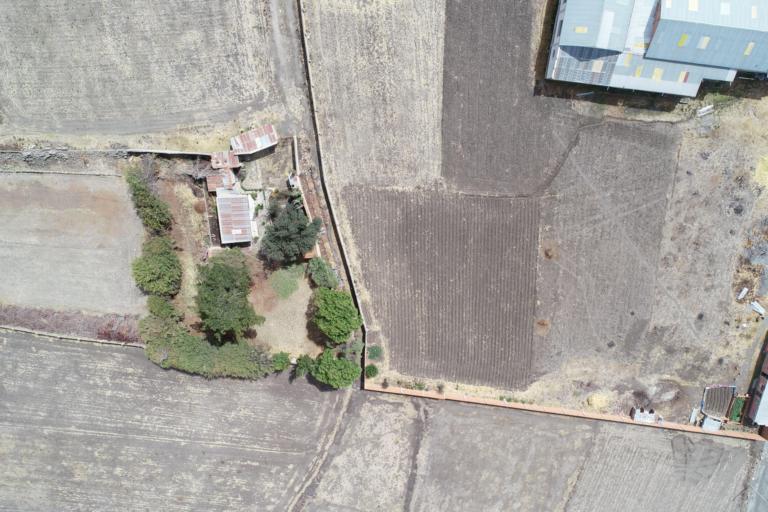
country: BO
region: La Paz
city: Achacachi
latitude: -16.0374
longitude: -68.6888
